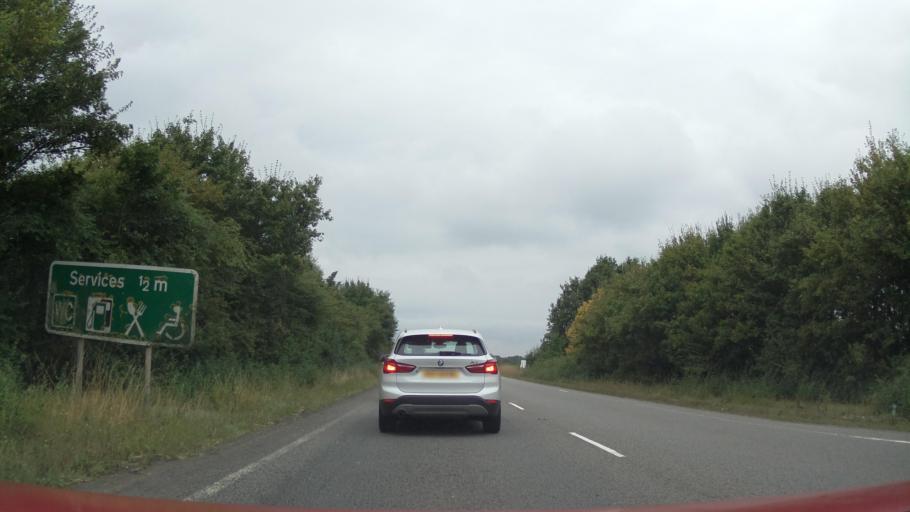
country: GB
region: England
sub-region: Nottinghamshire
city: South Collingham
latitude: 53.0930
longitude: -0.7710
